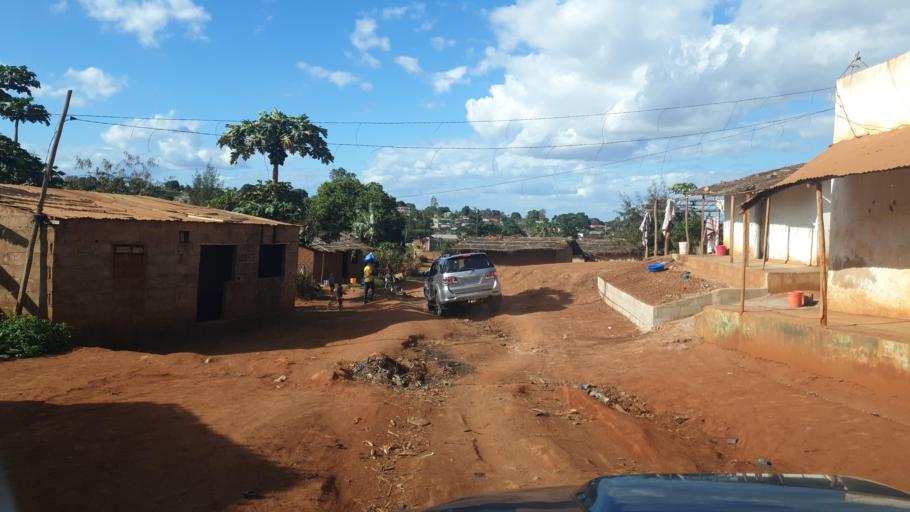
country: MZ
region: Nampula
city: Nampula
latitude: -15.0905
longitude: 39.2253
